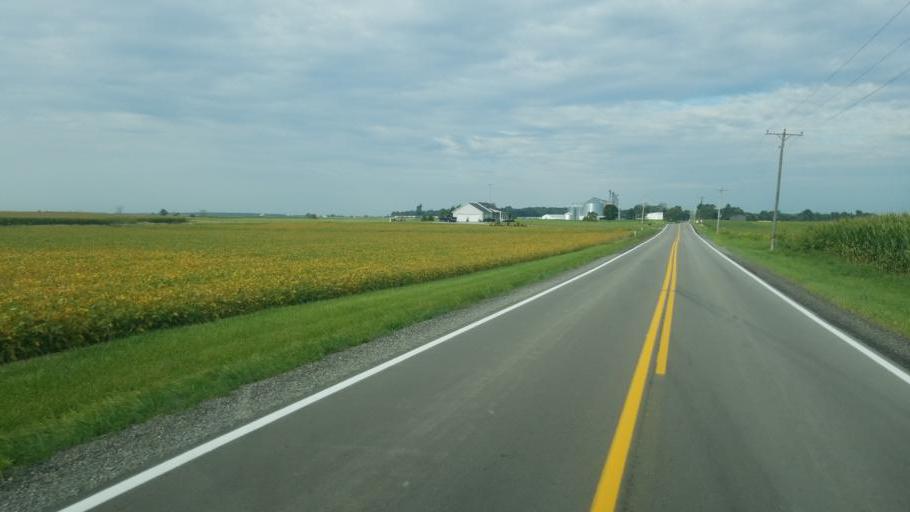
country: US
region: Ohio
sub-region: Crawford County
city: Bucyrus
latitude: 40.7177
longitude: -83.0265
